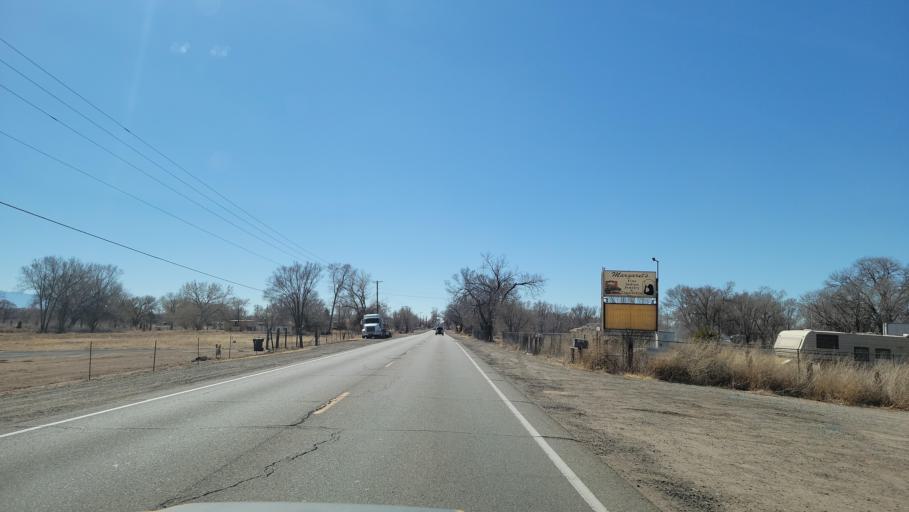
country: US
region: New Mexico
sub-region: Valencia County
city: Bosque Farms
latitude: 34.9253
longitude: -106.6929
